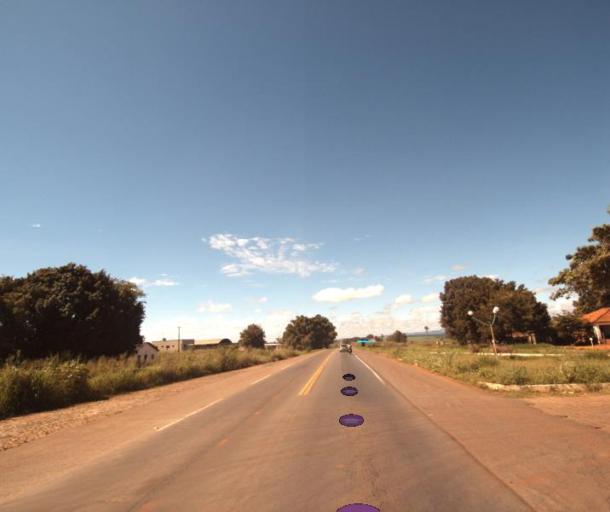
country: BR
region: Goias
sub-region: Rialma
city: Rialma
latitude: -15.3591
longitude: -49.5642
